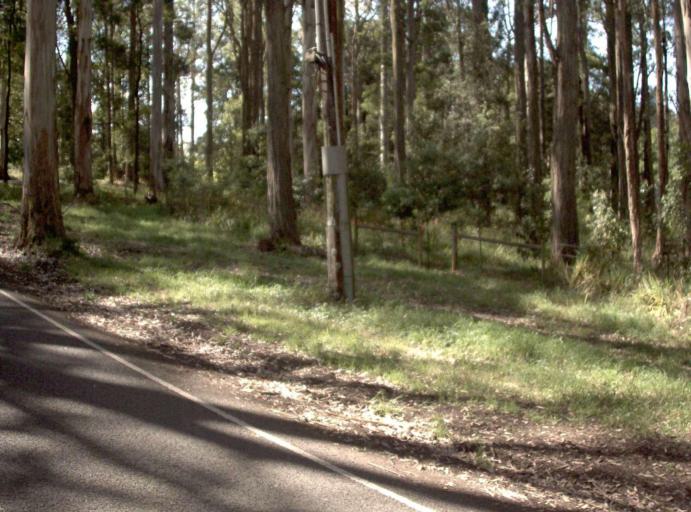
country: AU
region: Victoria
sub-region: Yarra Ranges
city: Mount Dandenong
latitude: -37.8357
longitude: 145.3501
